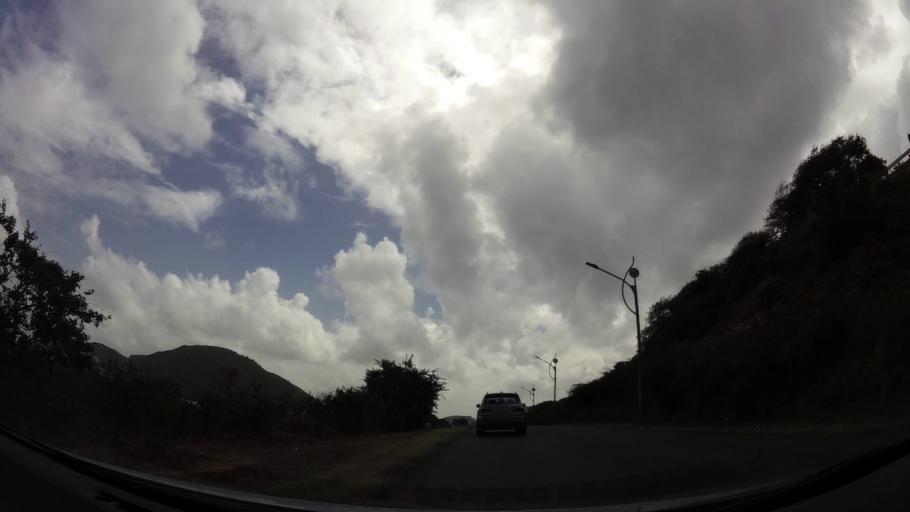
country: KN
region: Saint George Basseterre
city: Basseterre
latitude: 17.2879
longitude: -62.6928
